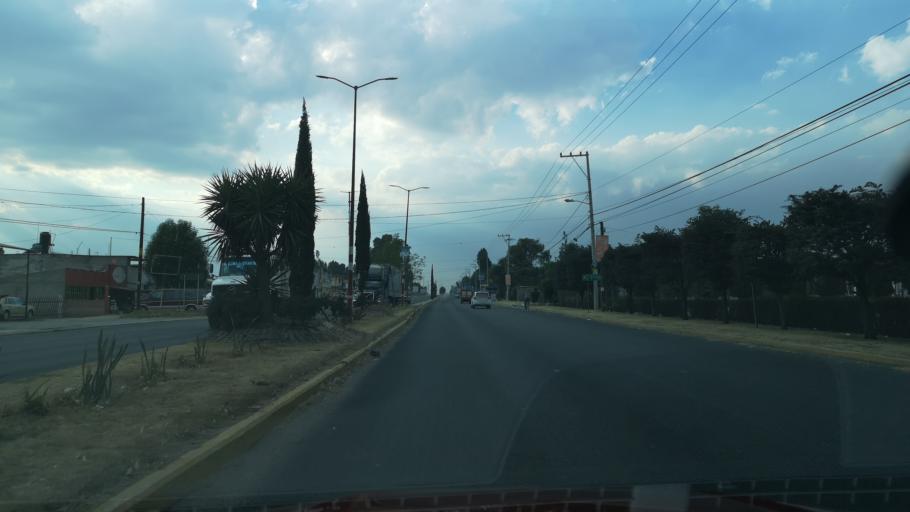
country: MX
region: Puebla
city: Cuanala
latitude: 19.1024
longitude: -98.3469
